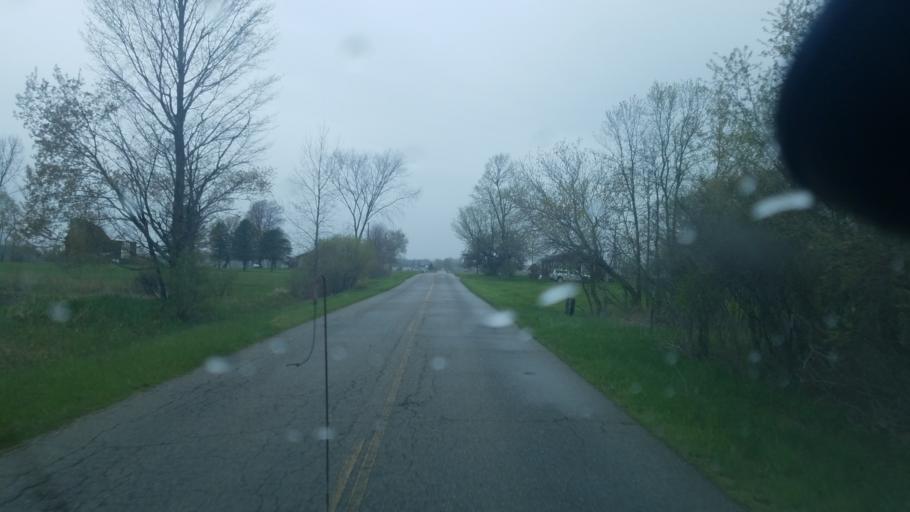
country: US
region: Michigan
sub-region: Montcalm County
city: Lakeview
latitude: 43.5110
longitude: -85.2937
